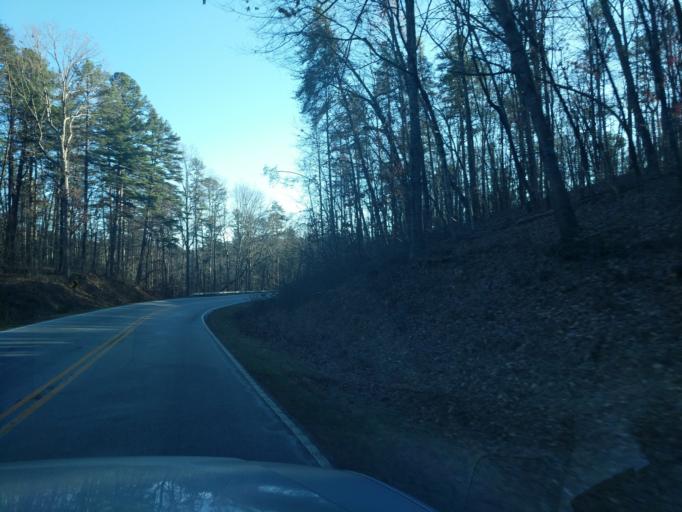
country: US
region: South Carolina
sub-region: Oconee County
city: Westminster
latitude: 34.7344
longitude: -83.2305
